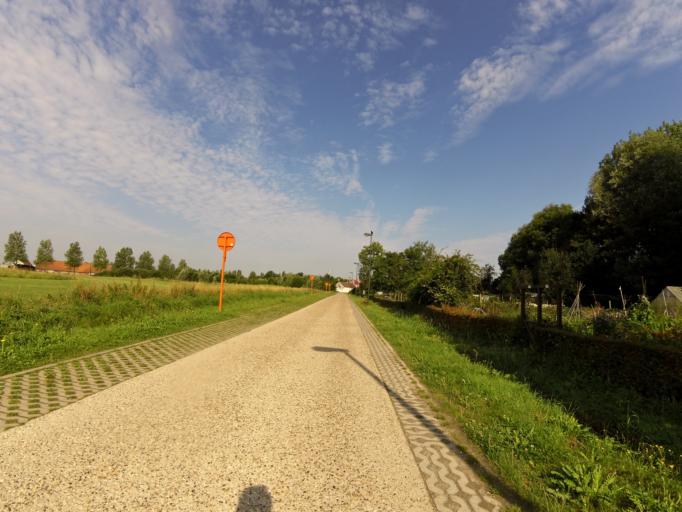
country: BE
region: Flanders
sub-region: Provincie West-Vlaanderen
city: Ostend
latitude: 51.2006
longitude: 2.9196
